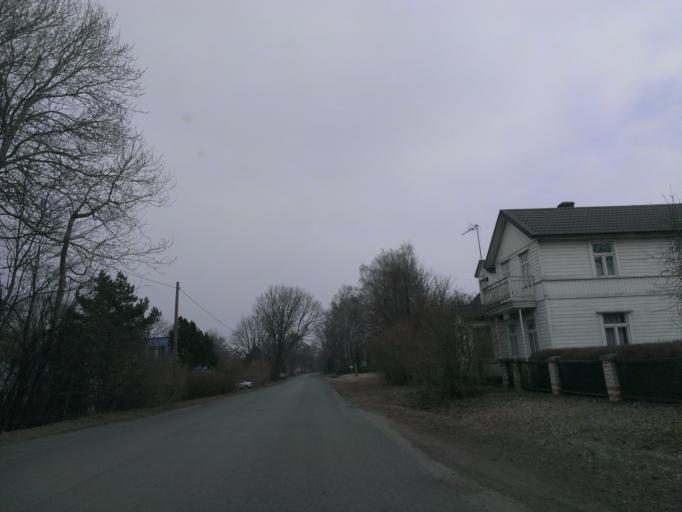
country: LV
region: Salacgrivas
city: Ainazi
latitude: 58.0023
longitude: 24.4386
